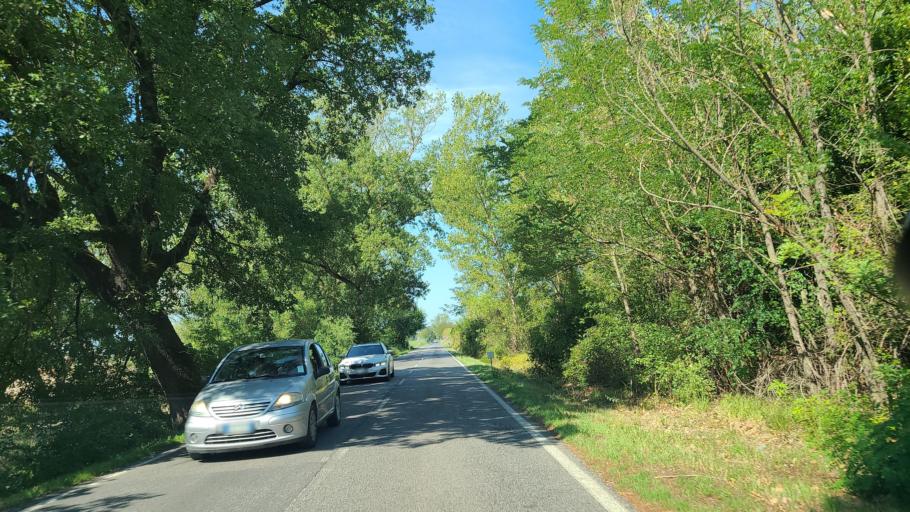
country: IT
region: Tuscany
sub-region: Provincia di Siena
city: Castellina Scalo
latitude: 43.3929
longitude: 11.2058
